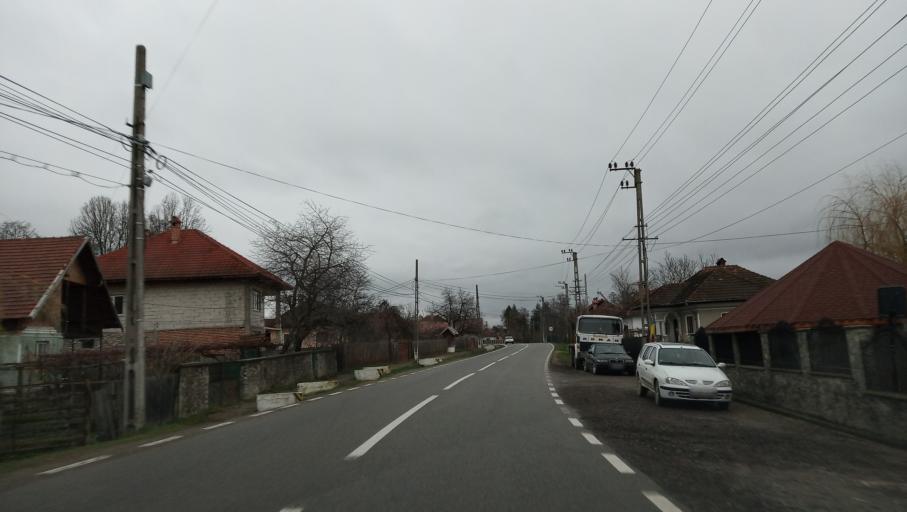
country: RO
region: Gorj
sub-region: Novaci
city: Pociovalistea
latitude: 45.1536
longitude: 23.6403
